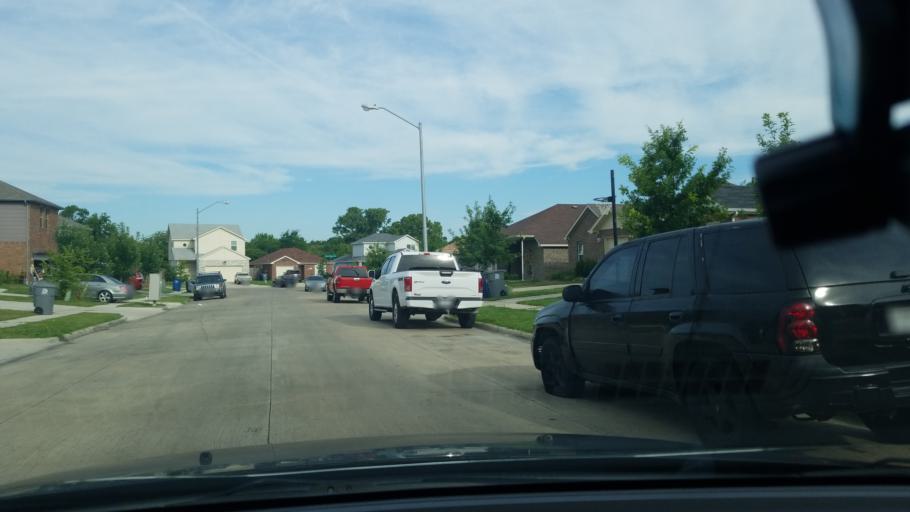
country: US
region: Texas
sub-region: Dallas County
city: Balch Springs
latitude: 32.7546
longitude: -96.6527
